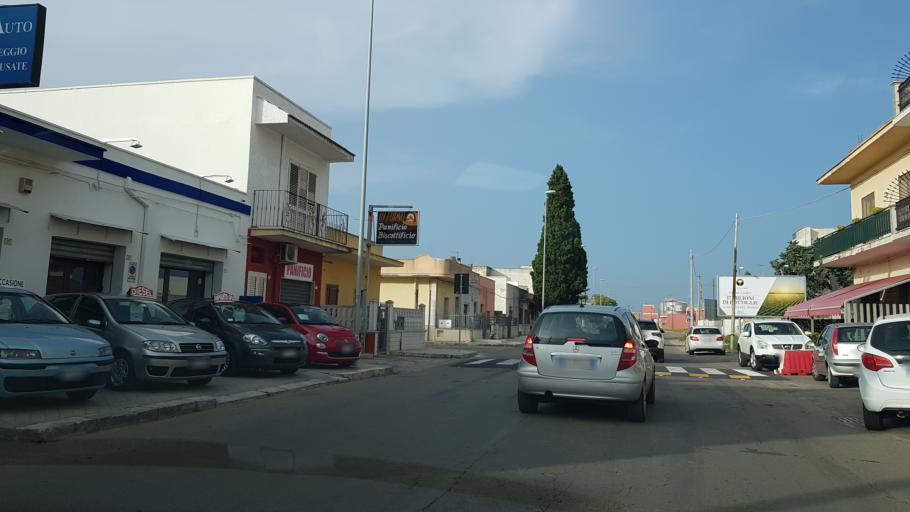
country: IT
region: Apulia
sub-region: Provincia di Brindisi
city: Cellino San Marco
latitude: 40.4762
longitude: 17.9755
